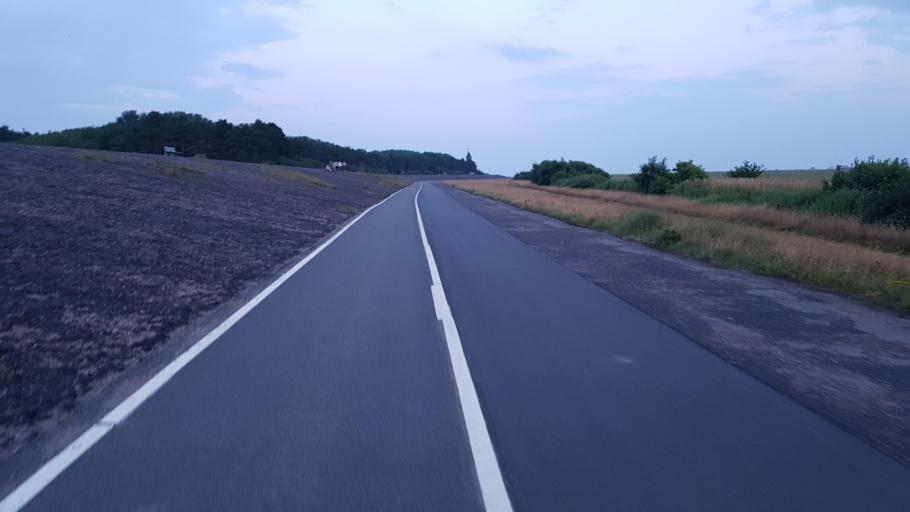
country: DE
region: Schleswig-Holstein
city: Sankt Peter-Ording
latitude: 54.2910
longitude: 8.6456
